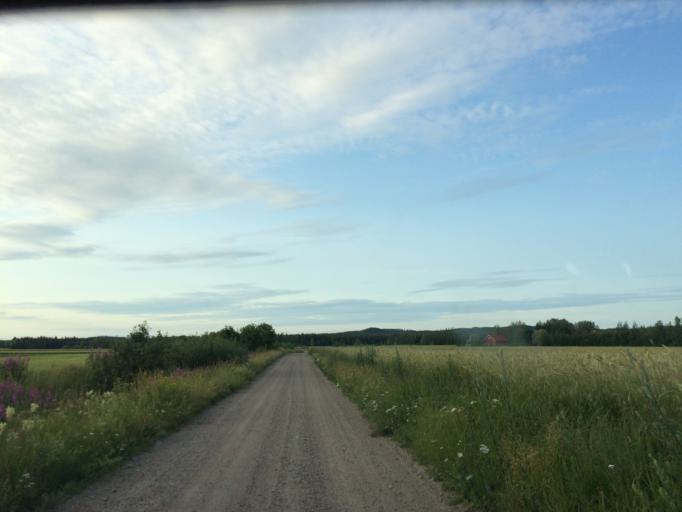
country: FI
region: Haeme
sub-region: Haemeenlinna
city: Turenki
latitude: 60.8830
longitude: 24.6312
